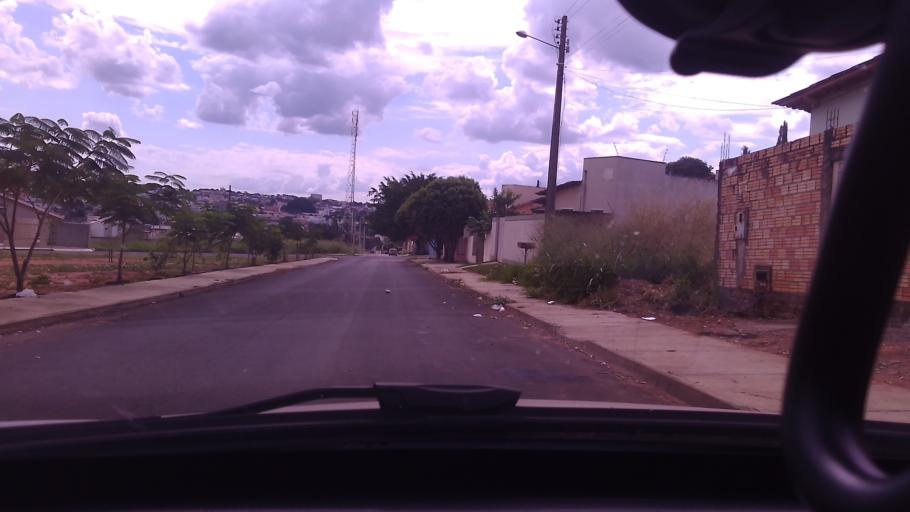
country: BR
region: Goias
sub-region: Mineiros
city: Mineiros
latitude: -17.5785
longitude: -52.5523
